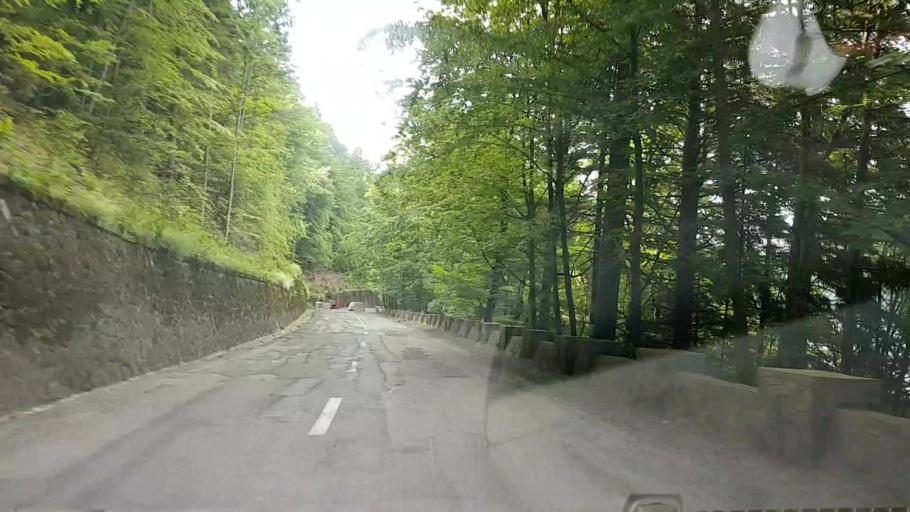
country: RO
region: Neamt
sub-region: Comuna Bicaz
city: Dodeni
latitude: 46.9359
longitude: 26.1201
